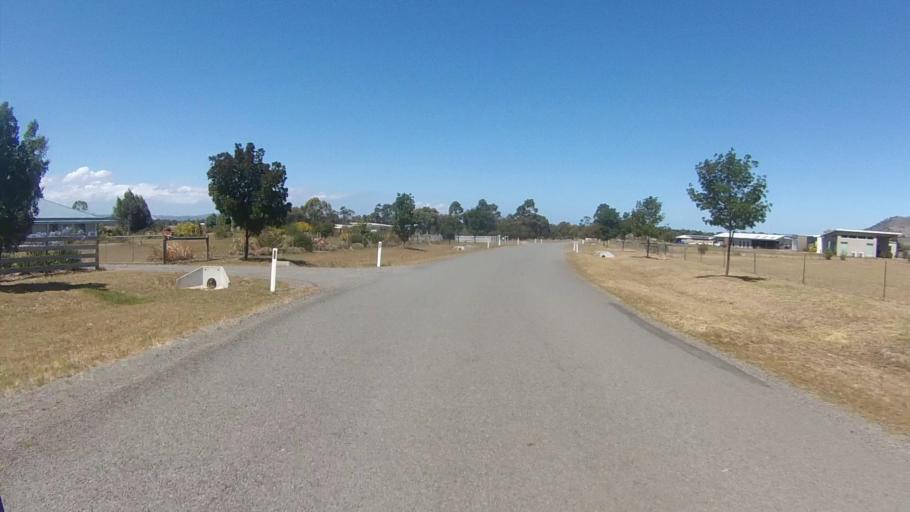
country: AU
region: Tasmania
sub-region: Clarence
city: Seven Mile Beach
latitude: -42.8427
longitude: 147.4782
